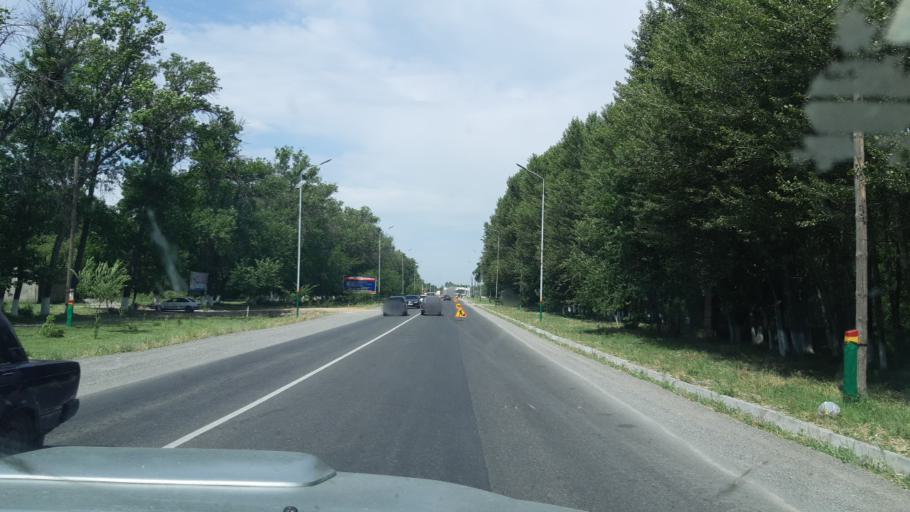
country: KZ
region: Ongtustik Qazaqstan
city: Turar Ryskulov
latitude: 42.5488
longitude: 70.3120
